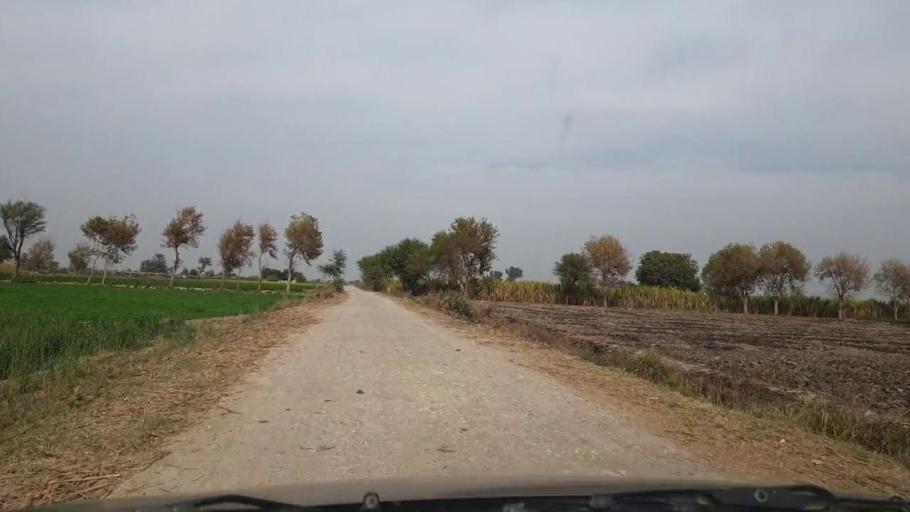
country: PK
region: Sindh
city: Sinjhoro
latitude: 26.0890
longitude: 68.8279
